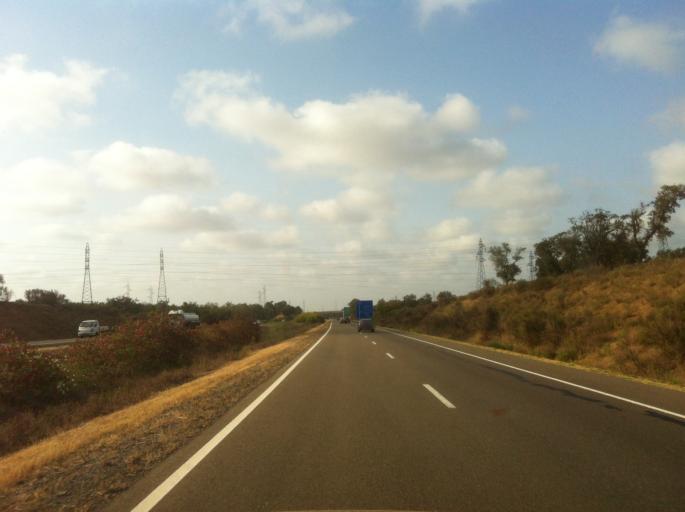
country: MA
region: Gharb-Chrarda-Beni Hssen
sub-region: Kenitra Province
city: Kenitra
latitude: 34.2232
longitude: -6.5437
